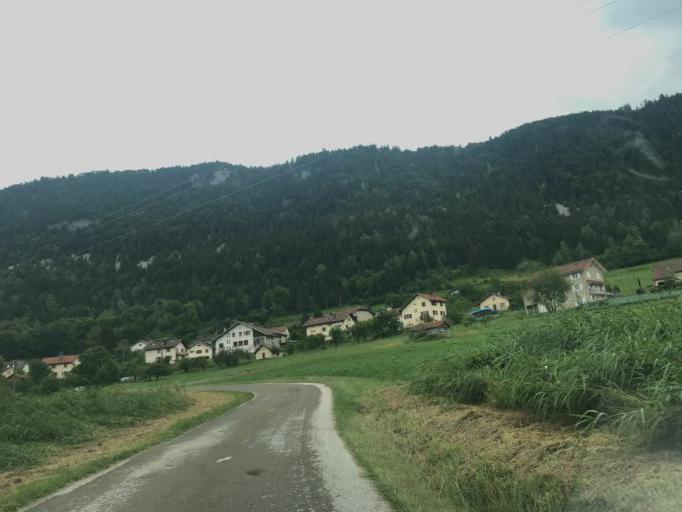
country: FR
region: Franche-Comte
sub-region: Departement du Jura
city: Saint-Claude
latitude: 46.3430
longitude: 5.8399
